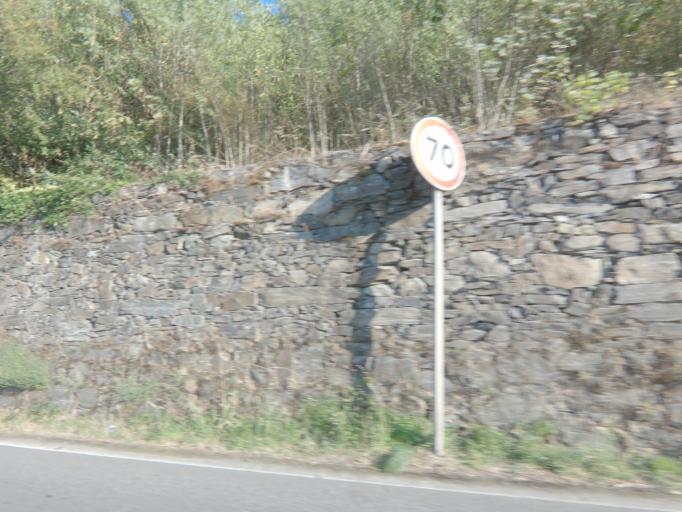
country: PT
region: Vila Real
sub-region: Peso da Regua
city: Peso da Regua
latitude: 41.1515
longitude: -7.7741
